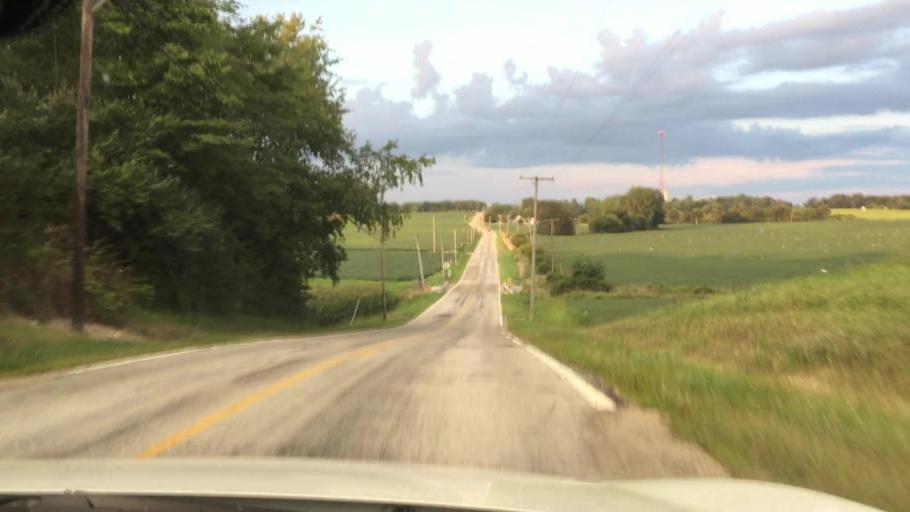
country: US
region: Ohio
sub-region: Champaign County
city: Mechanicsburg
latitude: 40.0067
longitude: -83.6080
